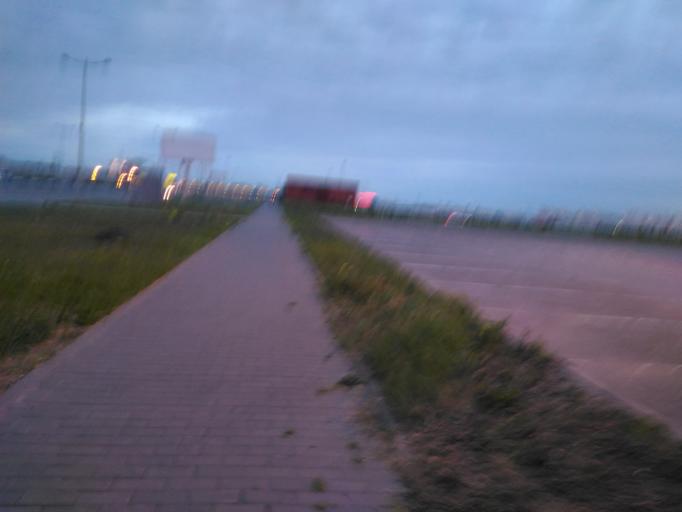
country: RU
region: Ulyanovsk
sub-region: Ulyanovskiy Rayon
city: Ulyanovsk
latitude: 54.2909
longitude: 48.2717
